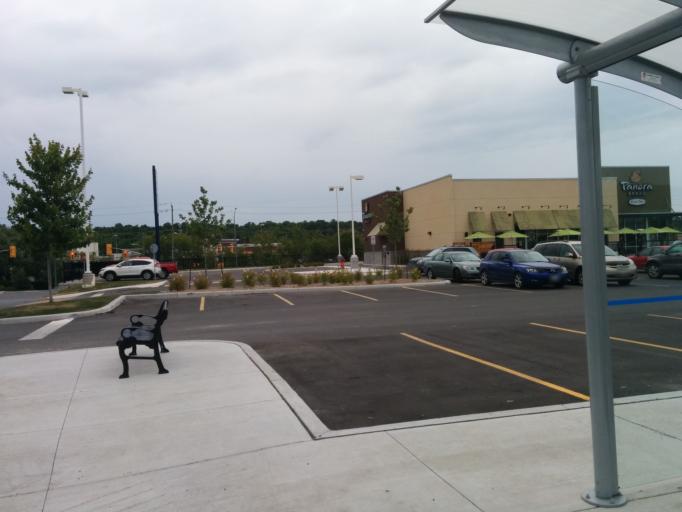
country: CA
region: Ontario
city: Kingston
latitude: 44.2649
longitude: -76.5027
